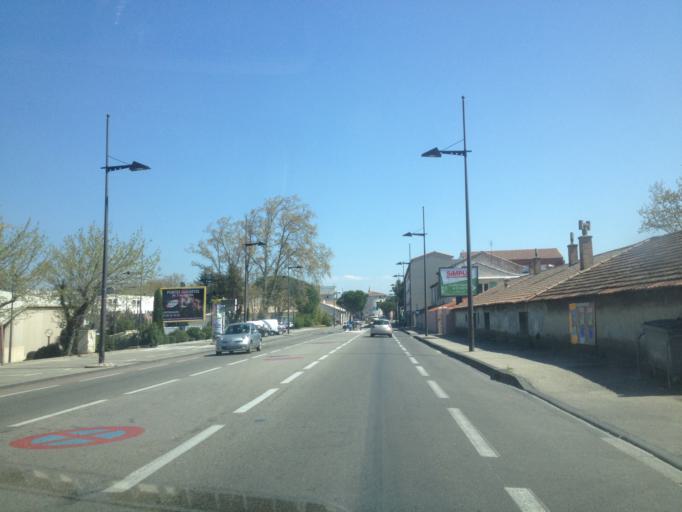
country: FR
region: Provence-Alpes-Cote d'Azur
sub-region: Departement du Vaucluse
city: Le Pontet
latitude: 43.9598
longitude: 4.8547
